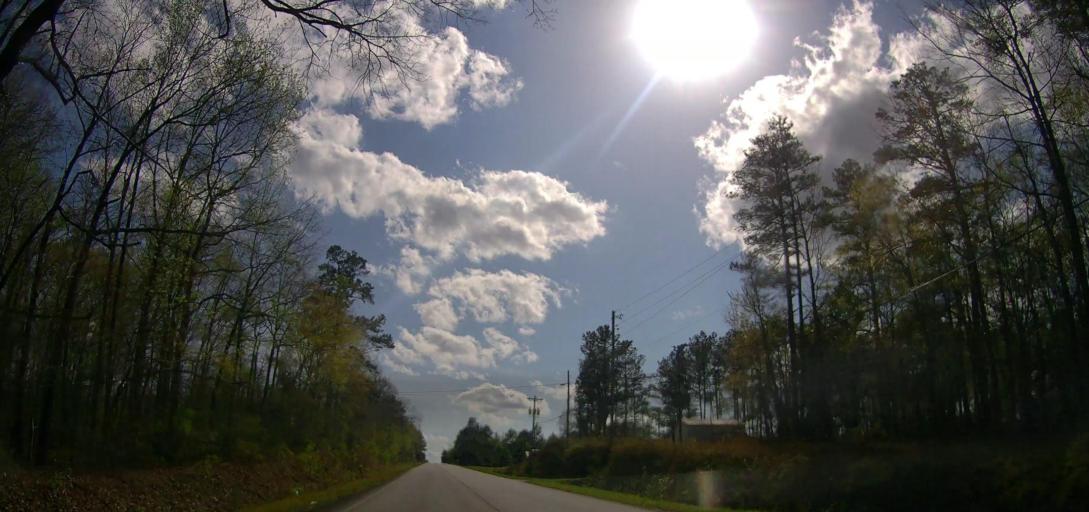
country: US
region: Georgia
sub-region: Baldwin County
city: Hardwick
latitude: 32.9880
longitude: -83.2690
